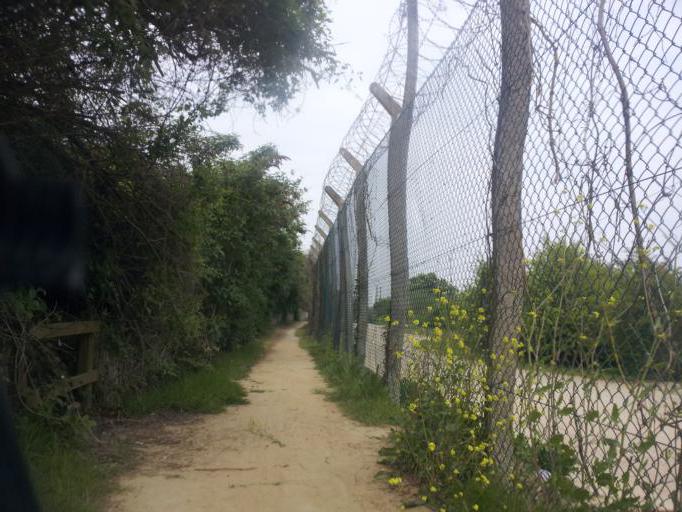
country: GB
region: England
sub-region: Medway
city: Rochester
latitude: 51.4027
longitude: 0.5219
